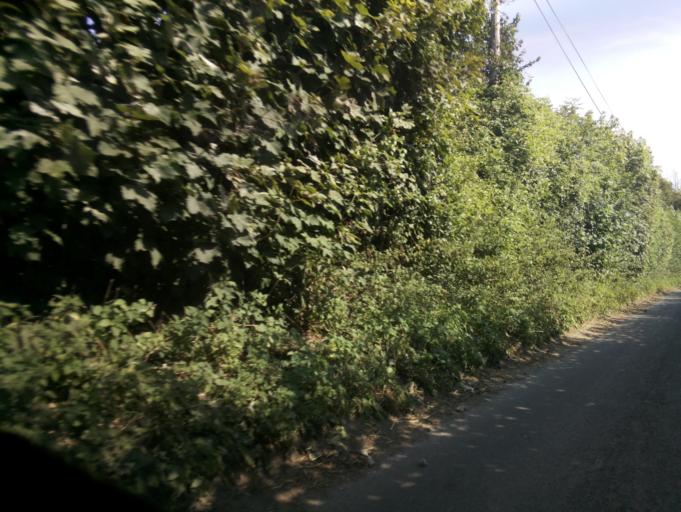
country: GB
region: England
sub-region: Gloucestershire
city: Dursley
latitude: 51.6863
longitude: -2.3200
